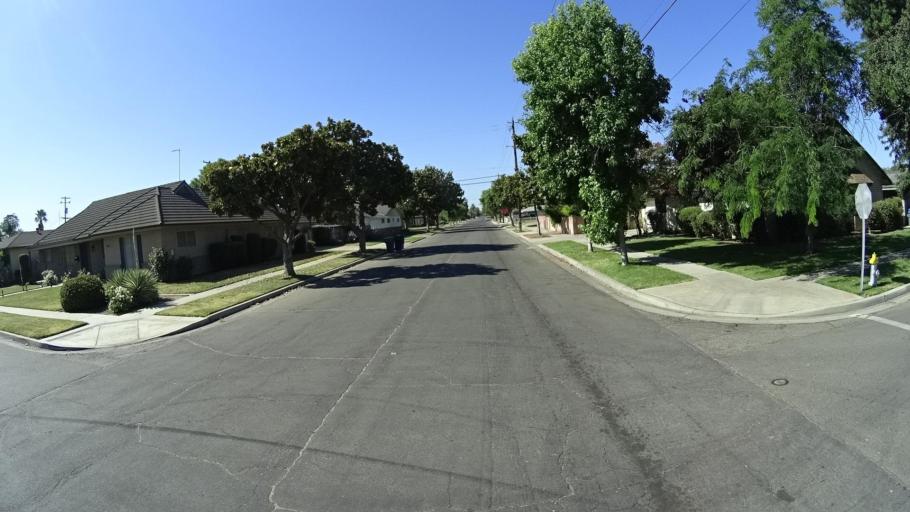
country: US
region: California
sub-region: Fresno County
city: Fresno
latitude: 36.7766
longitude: -119.8221
